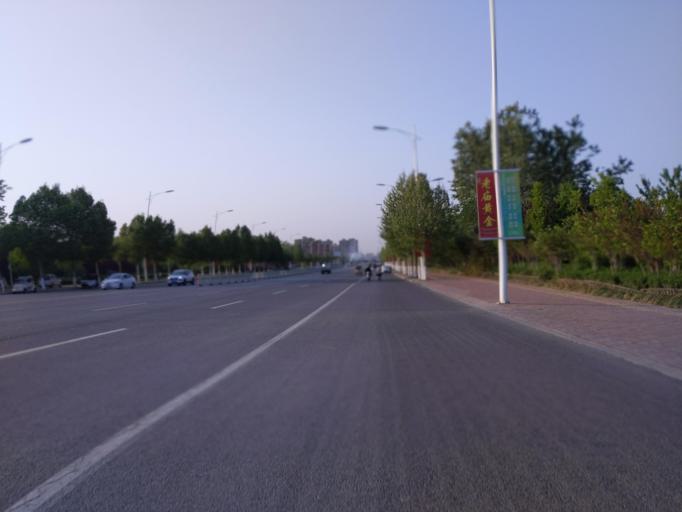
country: CN
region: Henan Sheng
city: Puyang Chengguanzhen
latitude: 35.6864
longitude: 115.0165
